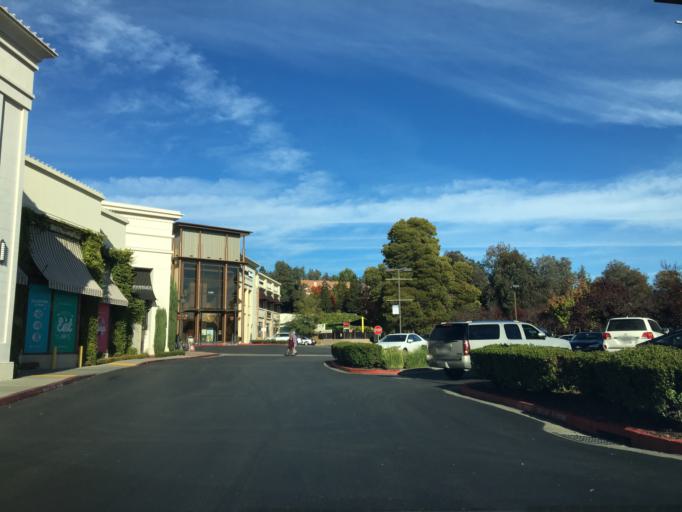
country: US
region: California
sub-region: Contra Costa County
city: Blackhawk
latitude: 37.8002
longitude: -121.9179
